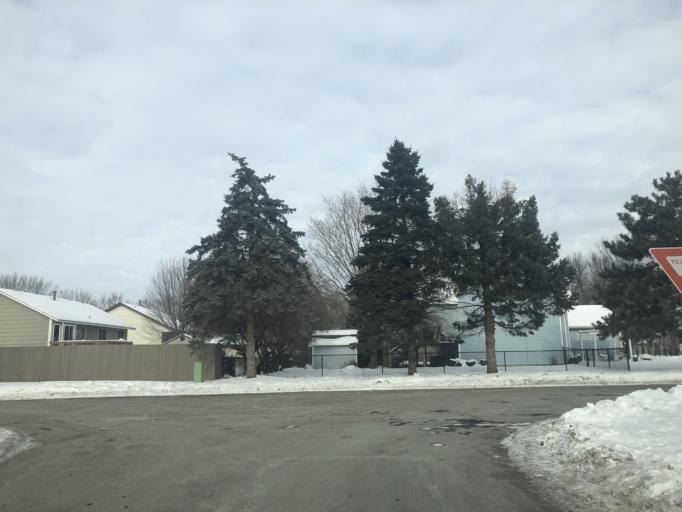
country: US
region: Minnesota
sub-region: Anoka County
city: Circle Pines
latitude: 45.1536
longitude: -93.1606
